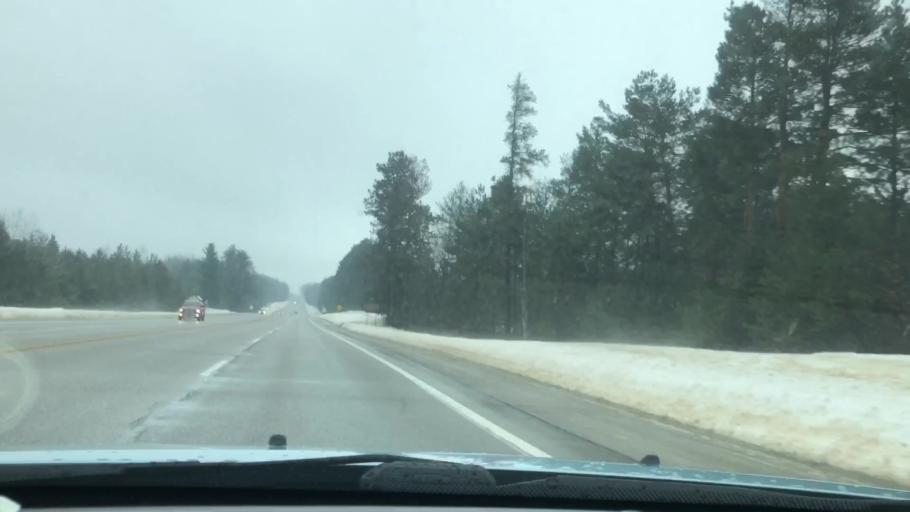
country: US
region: Michigan
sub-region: Otsego County
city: Gaylord
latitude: 45.0449
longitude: -84.7759
